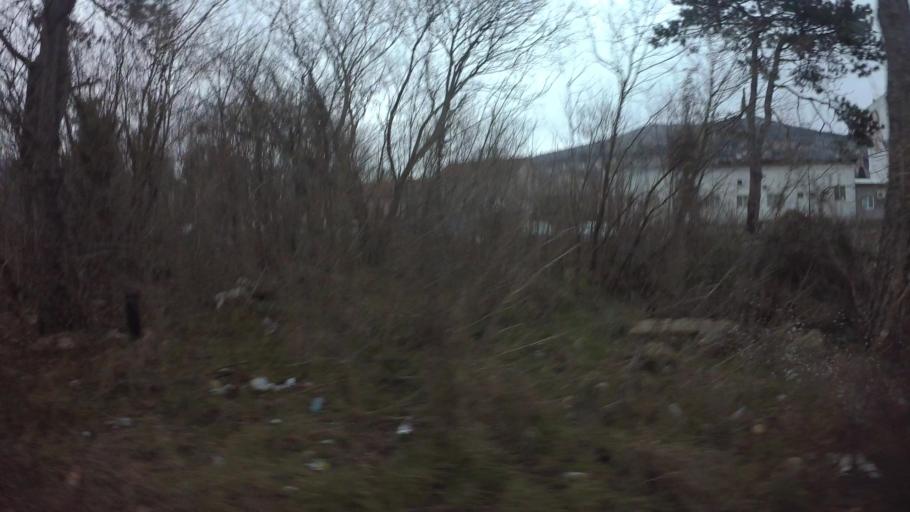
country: BA
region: Federation of Bosnia and Herzegovina
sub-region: Hercegovacko-Bosanski Kanton
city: Mostar
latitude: 43.3507
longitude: 17.8115
